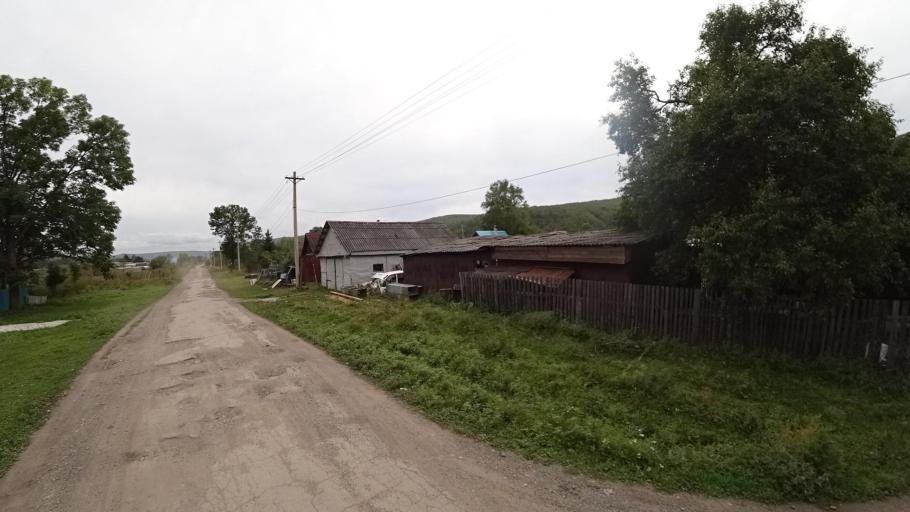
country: RU
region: Jewish Autonomous Oblast
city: Khingansk
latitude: 49.0384
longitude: 131.0496
